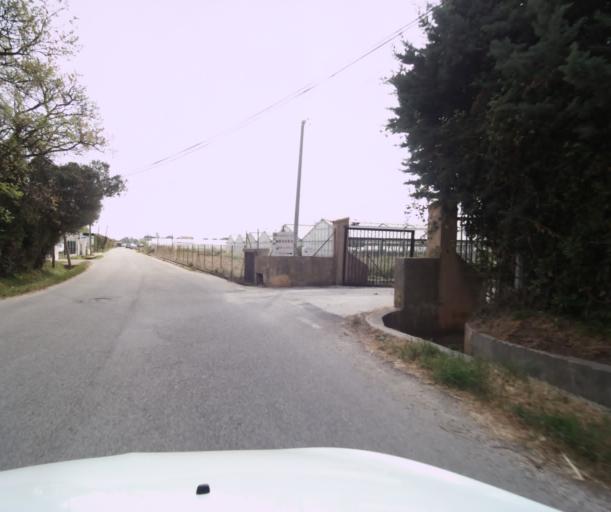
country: FR
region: Provence-Alpes-Cote d'Azur
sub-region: Departement du Var
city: Hyeres
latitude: 43.0940
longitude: 6.1361
